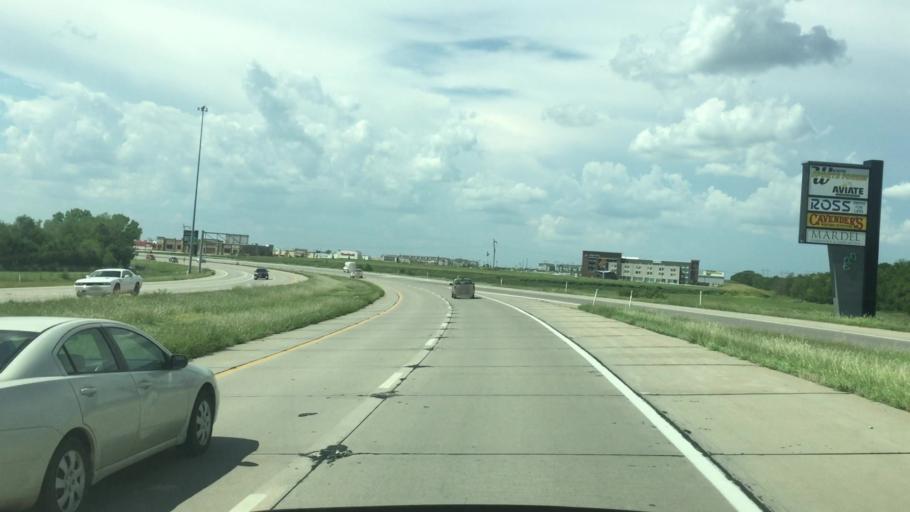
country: US
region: Kansas
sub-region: Butler County
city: Andover
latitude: 37.7256
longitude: -97.1994
